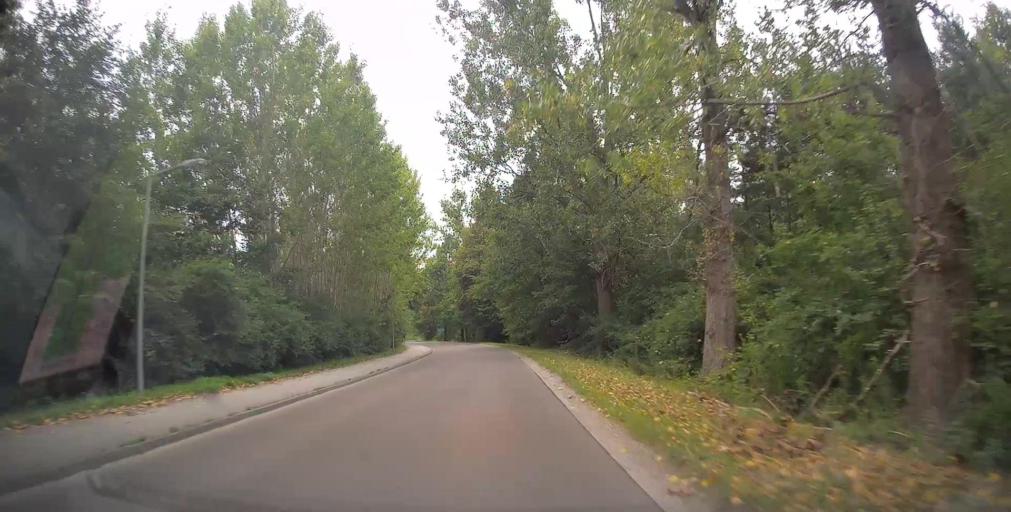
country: PL
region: Masovian Voivodeship
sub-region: Powiat bialobrzeski
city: Sucha
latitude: 51.6327
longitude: 20.9538
